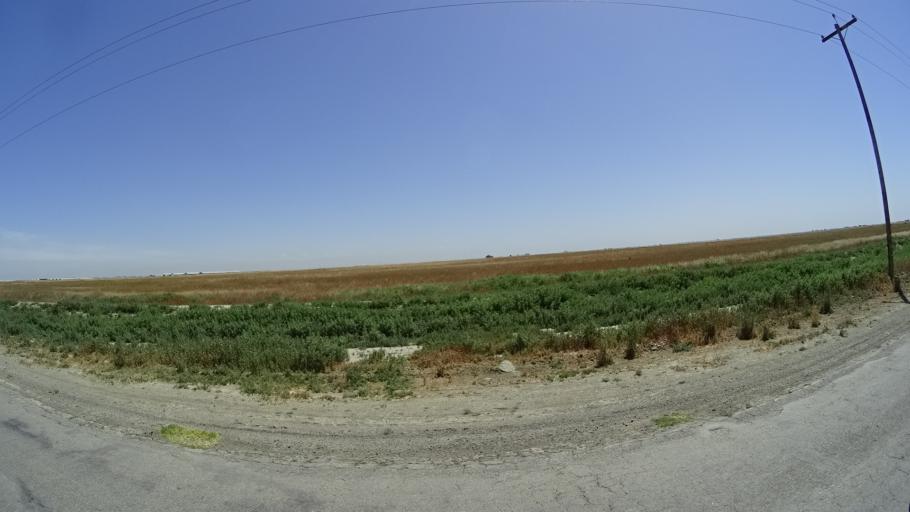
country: US
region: California
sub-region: Kings County
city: Stratford
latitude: 36.1540
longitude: -119.7174
